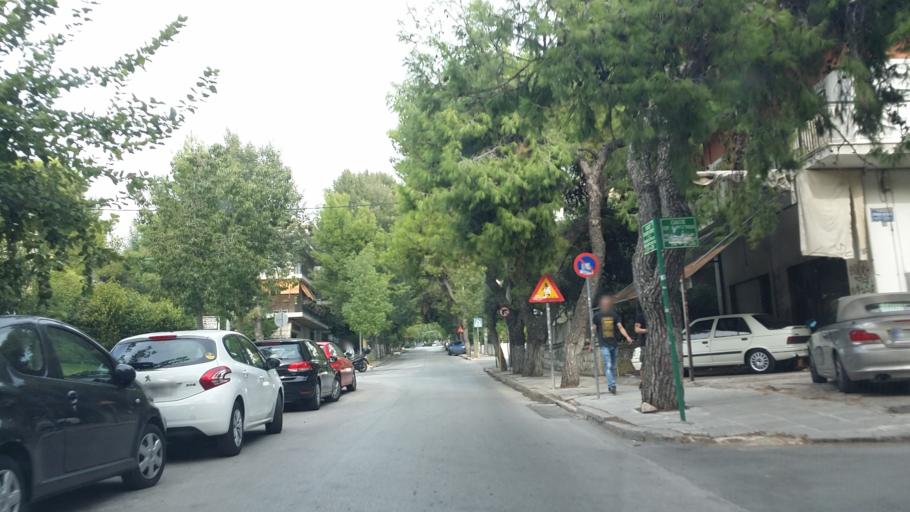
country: GR
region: Attica
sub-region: Nomarchia Athinas
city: Irakleio
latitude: 38.0490
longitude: 23.7686
